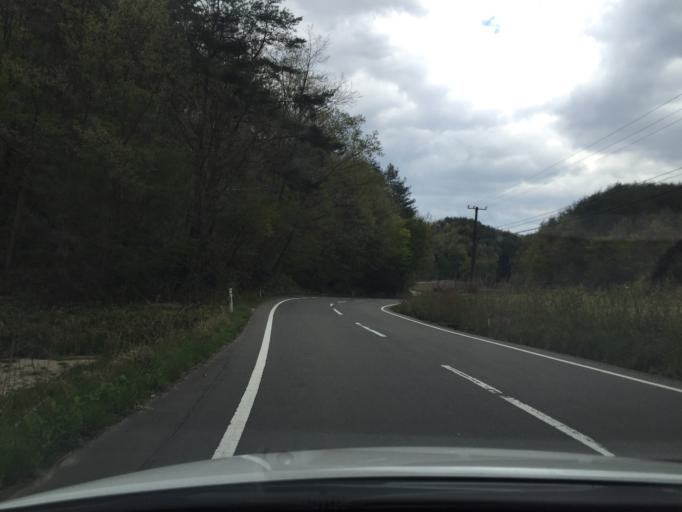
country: JP
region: Fukushima
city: Yanagawamachi-saiwaicho
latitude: 37.7207
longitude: 140.7318
